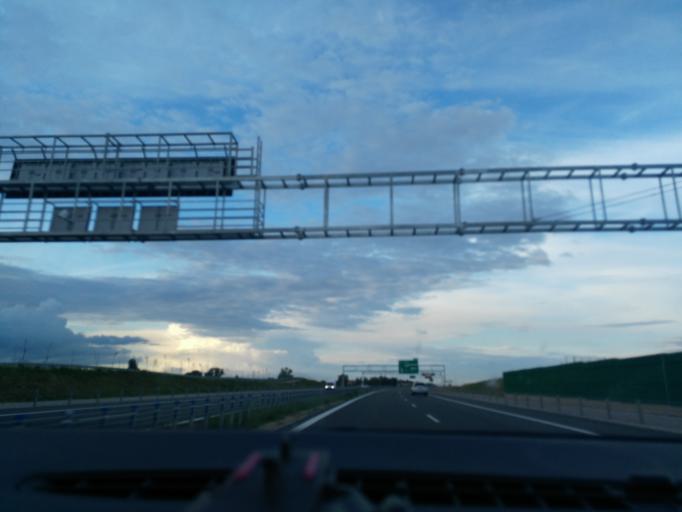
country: PL
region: Lublin Voivodeship
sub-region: Powiat lubelski
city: Jastkow
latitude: 51.2739
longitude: 22.4325
